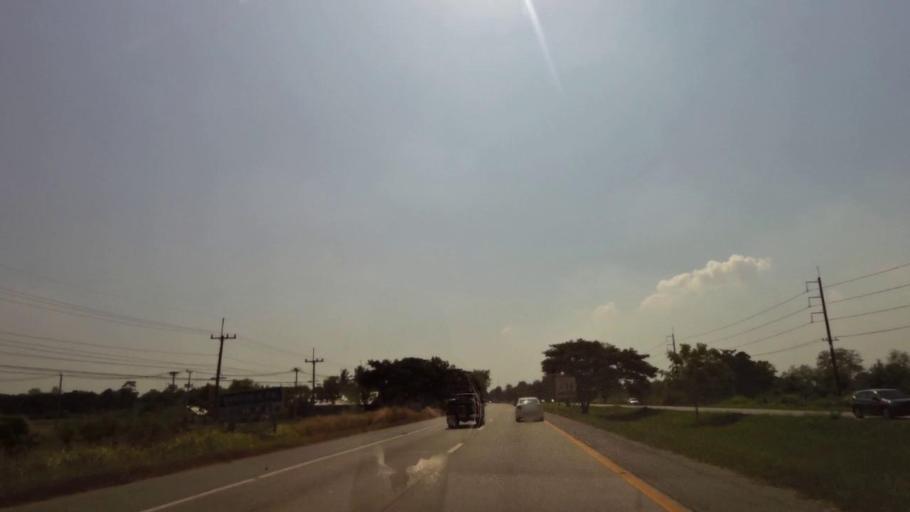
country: TH
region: Phichit
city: Wachira Barami
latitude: 16.5898
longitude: 100.1471
